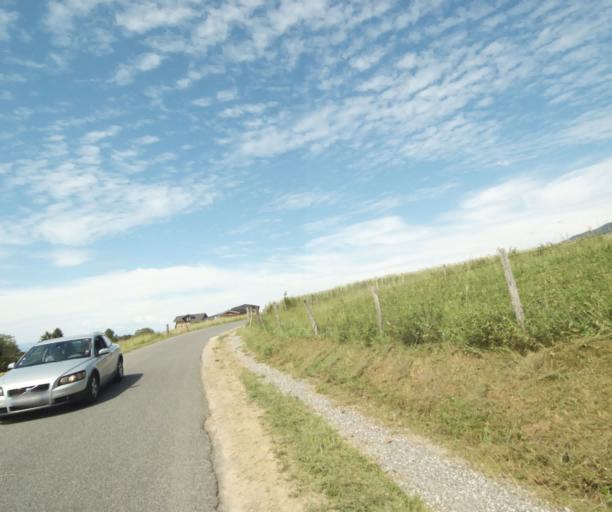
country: FR
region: Rhone-Alpes
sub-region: Departement de la Haute-Savoie
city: Bons-en-Chablais
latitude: 46.2804
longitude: 6.4135
